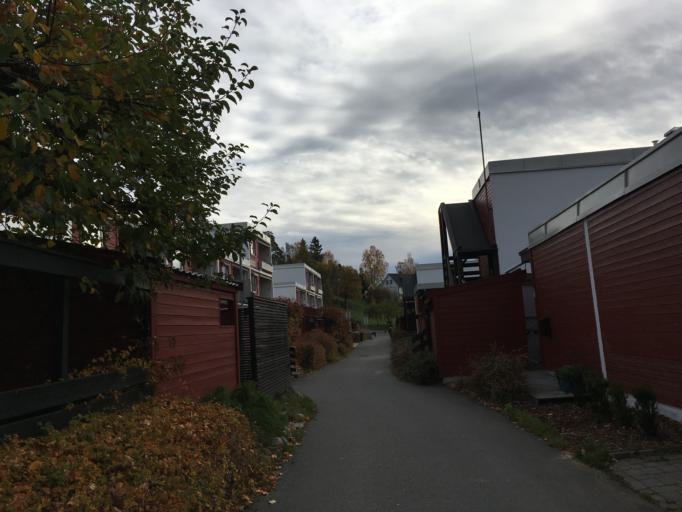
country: NO
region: Akershus
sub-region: Baerum
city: Lysaker
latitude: 59.9347
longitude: 10.6375
